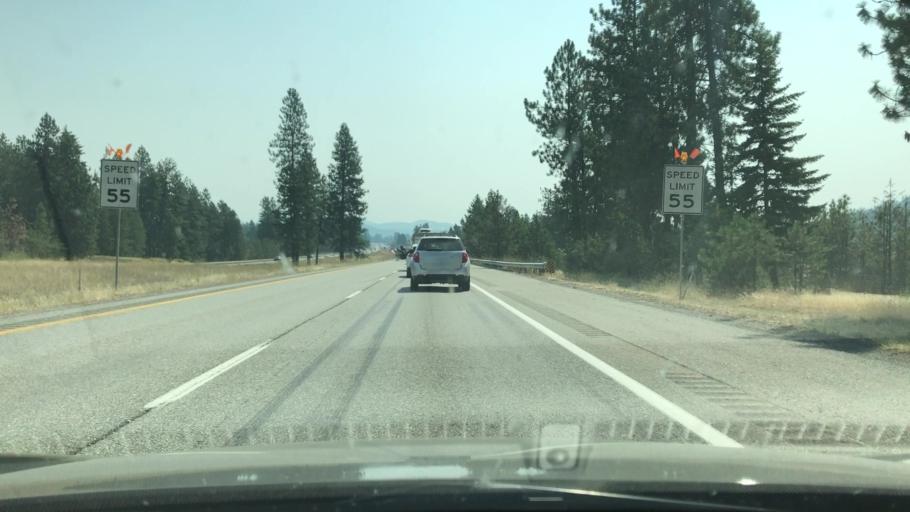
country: US
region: Idaho
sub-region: Kootenai County
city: Coeur d'Alene
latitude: 47.7045
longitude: -116.8374
